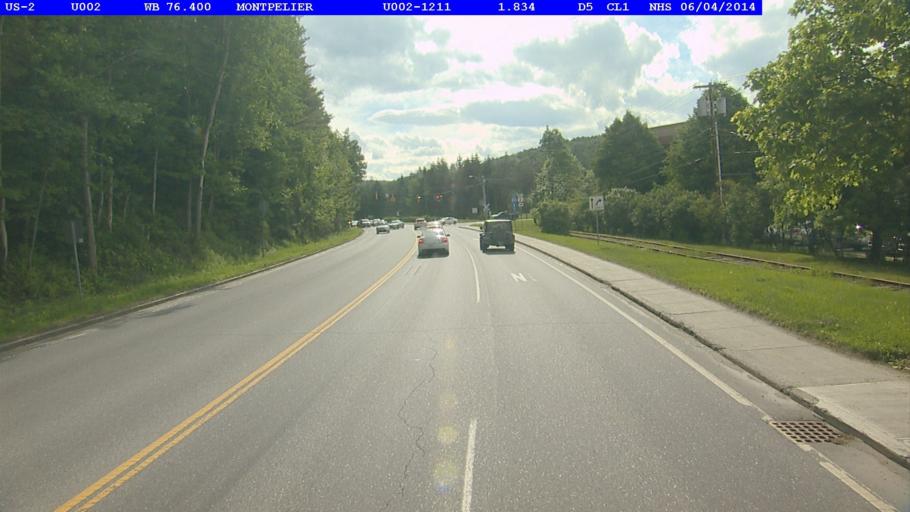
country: US
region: Vermont
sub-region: Washington County
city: Montpelier
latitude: 44.2603
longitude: -72.5836
